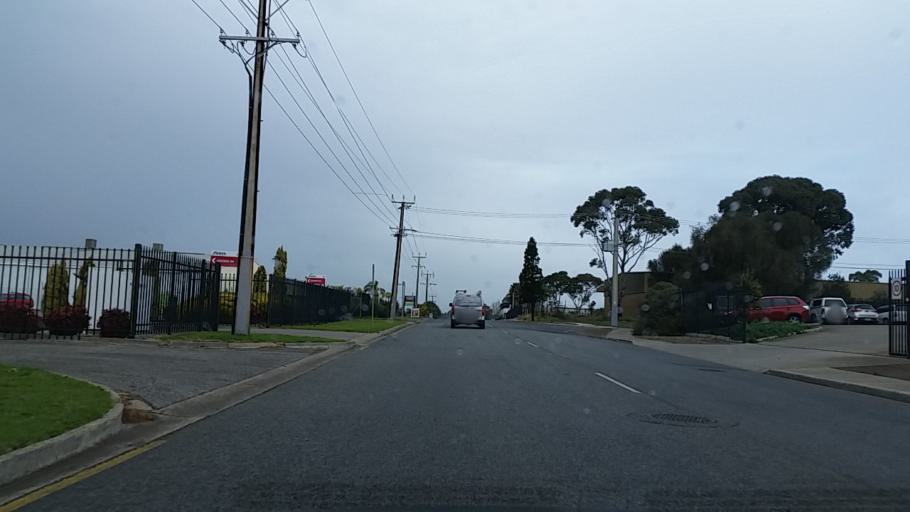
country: AU
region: South Australia
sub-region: Onkaparinga
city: Morphett Vale
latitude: -35.1124
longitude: 138.5074
